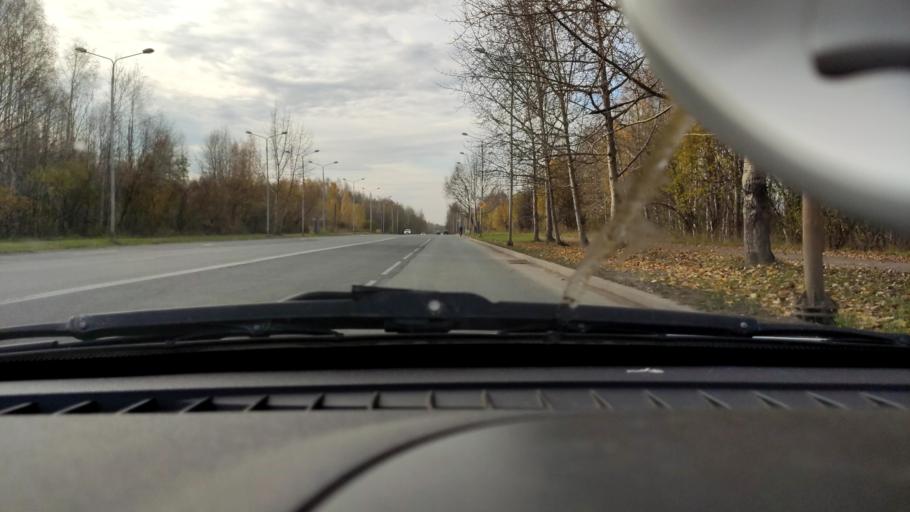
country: RU
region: Perm
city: Perm
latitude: 58.1101
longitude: 56.3982
